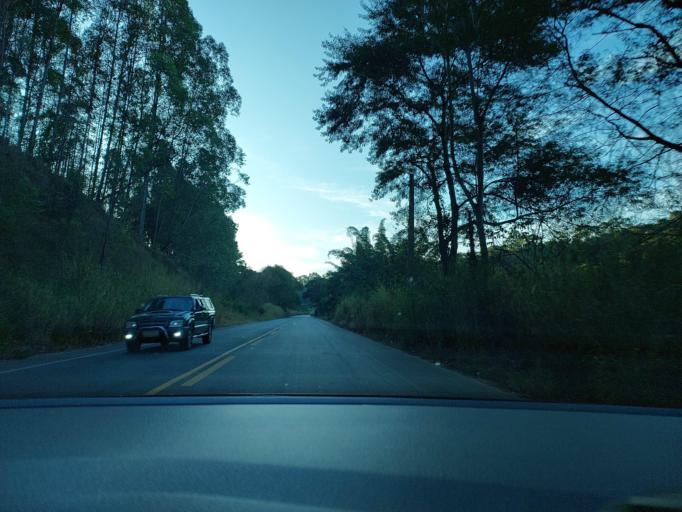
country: BR
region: Minas Gerais
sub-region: Vicosa
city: Vicosa
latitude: -20.8180
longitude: -42.8244
